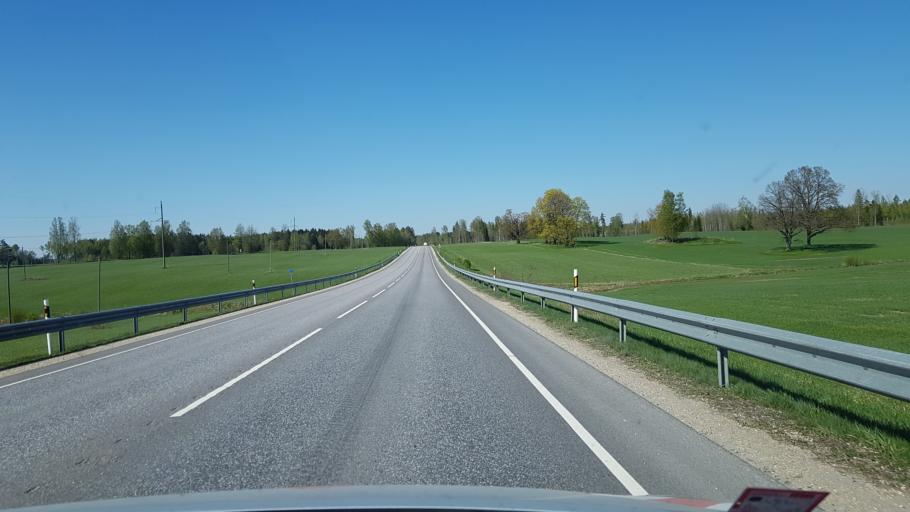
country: EE
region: Vorumaa
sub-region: Antsla vald
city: Vana-Antsla
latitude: 57.9911
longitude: 26.7658
